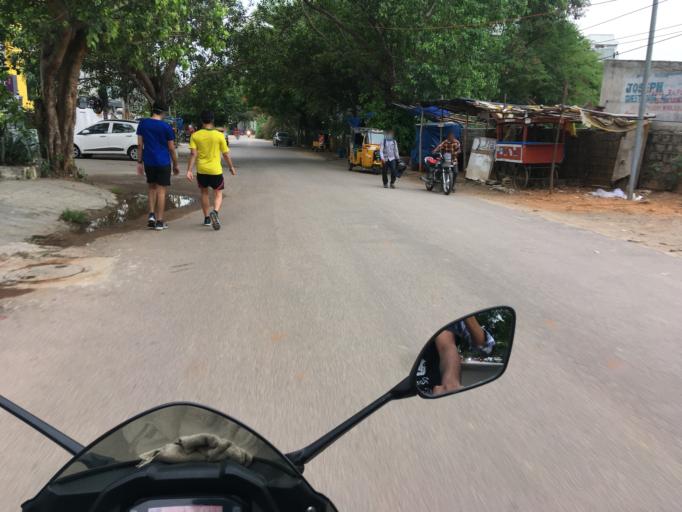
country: IN
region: Telangana
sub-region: Rangareddi
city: Kukatpalli
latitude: 17.4488
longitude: 78.3858
